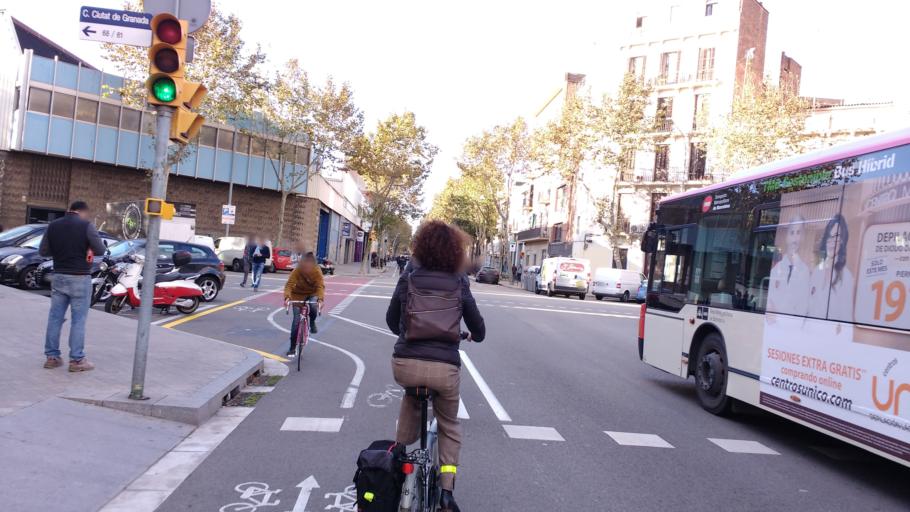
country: ES
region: Catalonia
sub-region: Provincia de Barcelona
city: Sant Marti
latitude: 41.3992
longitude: 2.1975
